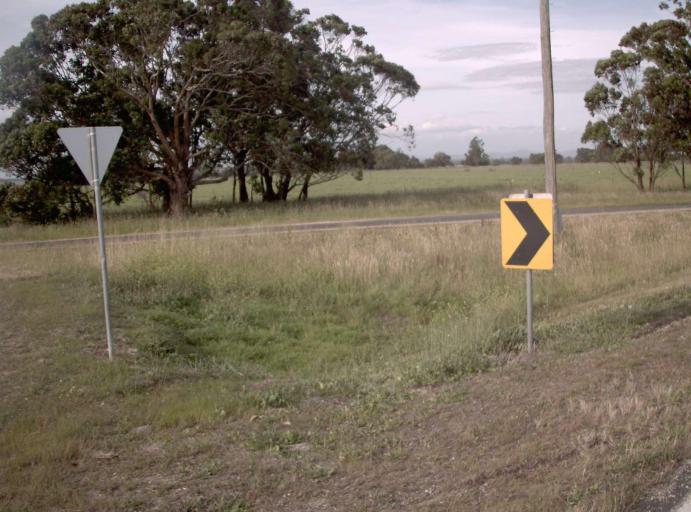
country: AU
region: Victoria
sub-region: Wellington
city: Heyfield
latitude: -38.0121
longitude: 146.6728
